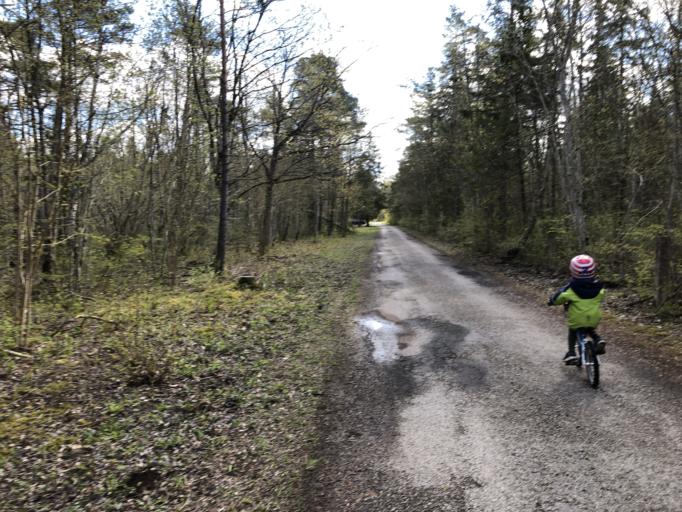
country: EE
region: Harju
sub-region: Harku vald
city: Tabasalu
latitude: 59.4374
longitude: 24.5349
